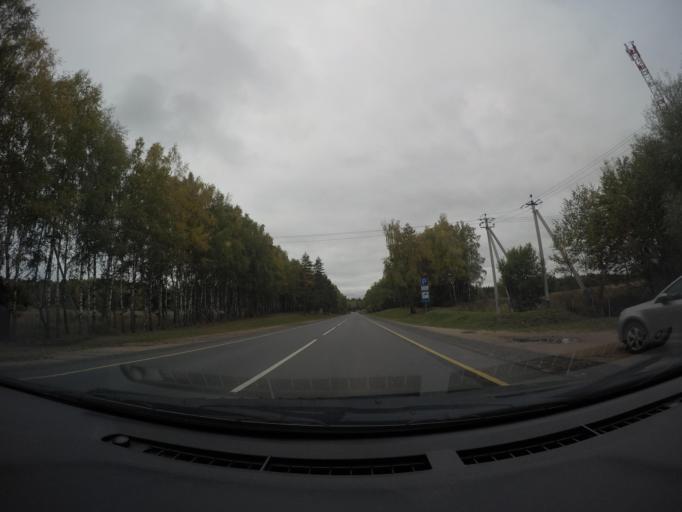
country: RU
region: Moskovskaya
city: Ruza
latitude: 55.7572
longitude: 36.2596
